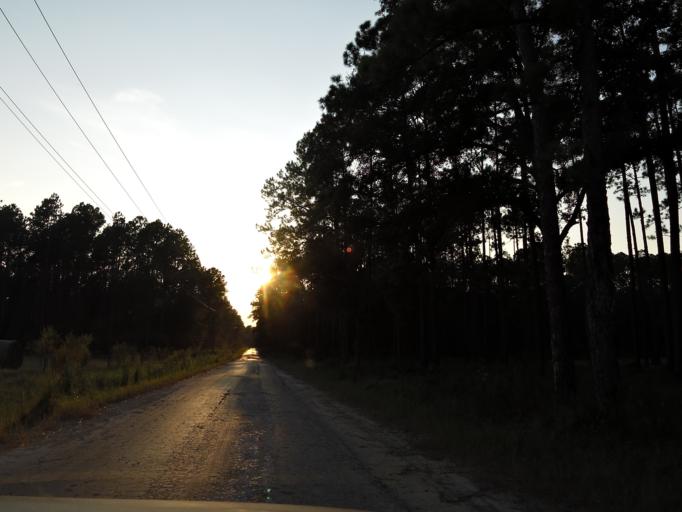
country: US
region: Florida
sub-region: Baker County
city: Macclenny
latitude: 30.3837
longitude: -82.0708
